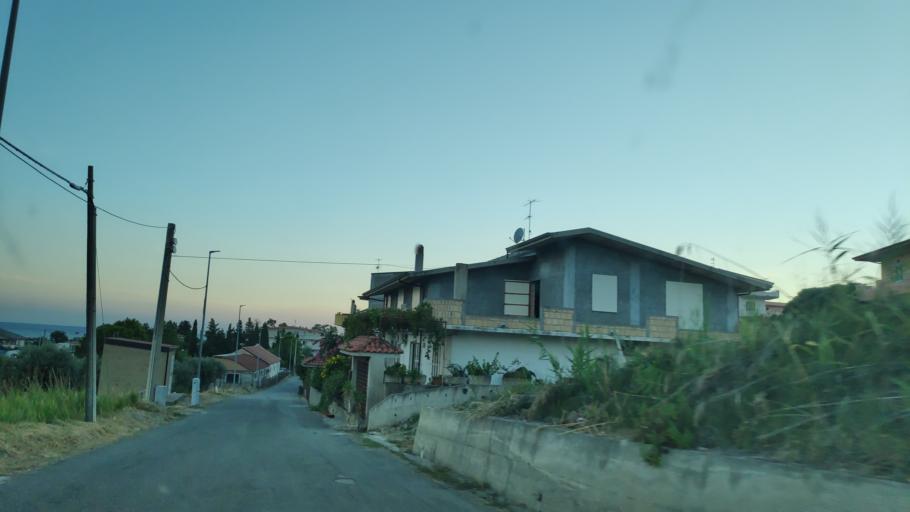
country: IT
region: Calabria
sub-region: Provincia di Reggio Calabria
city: Riace Marina
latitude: 38.3902
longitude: 16.5284
